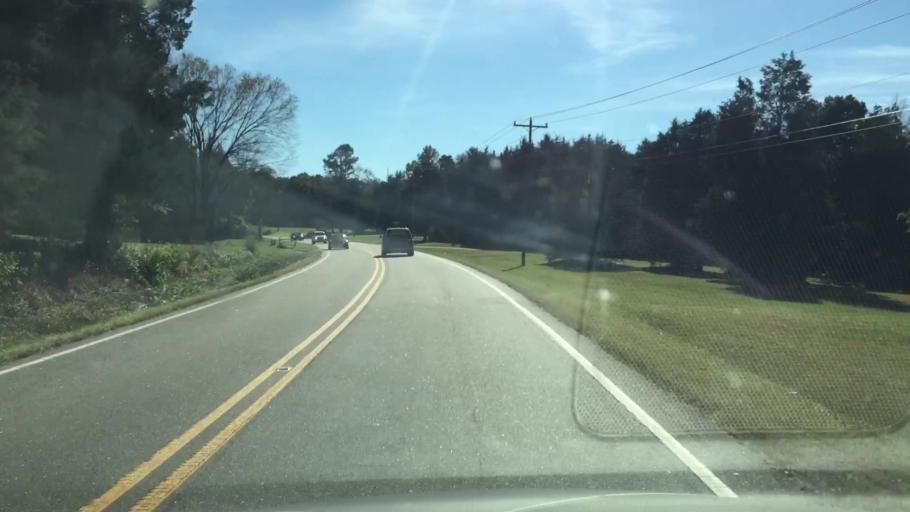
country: US
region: North Carolina
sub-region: Iredell County
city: Mooresville
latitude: 35.6121
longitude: -80.7546
